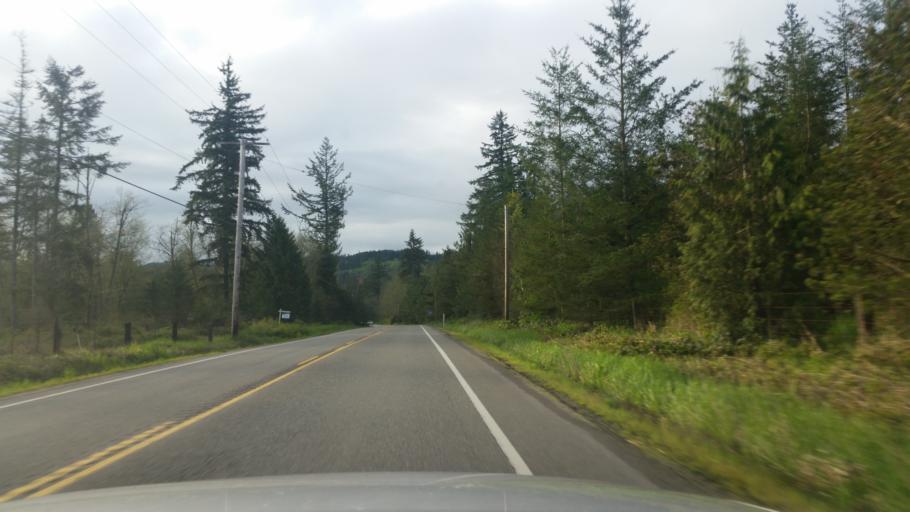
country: US
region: Washington
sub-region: Pierce County
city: Eatonville
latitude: 46.9459
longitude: -122.2883
